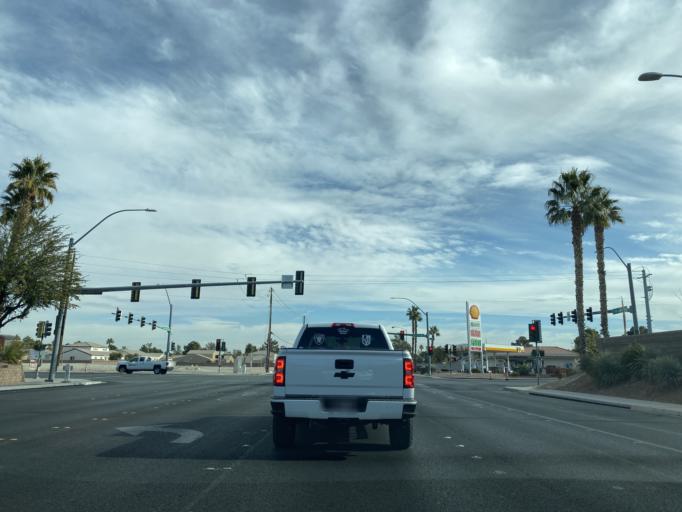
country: US
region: Nevada
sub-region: Clark County
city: Las Vegas
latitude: 36.2467
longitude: -115.2083
